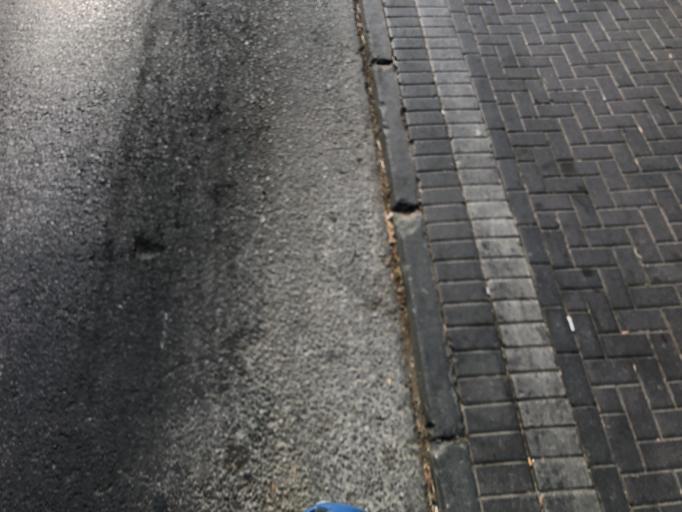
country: IL
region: Central District
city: Yehud
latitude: 32.0282
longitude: 34.8872
